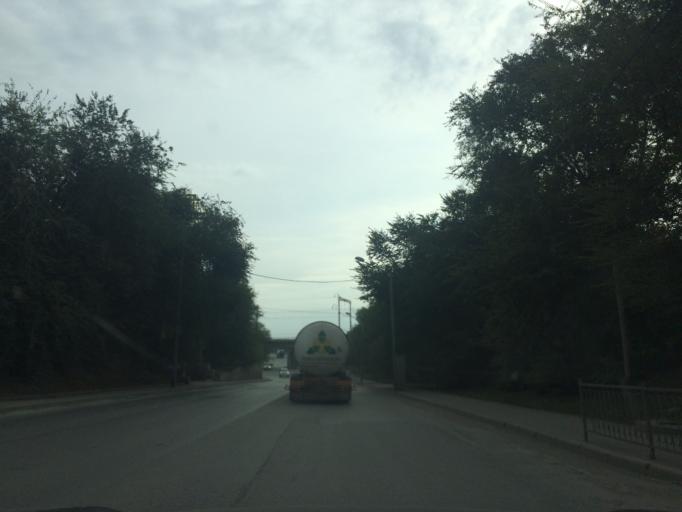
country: RU
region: Rostov
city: Kalinin
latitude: 47.1979
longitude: 39.6136
